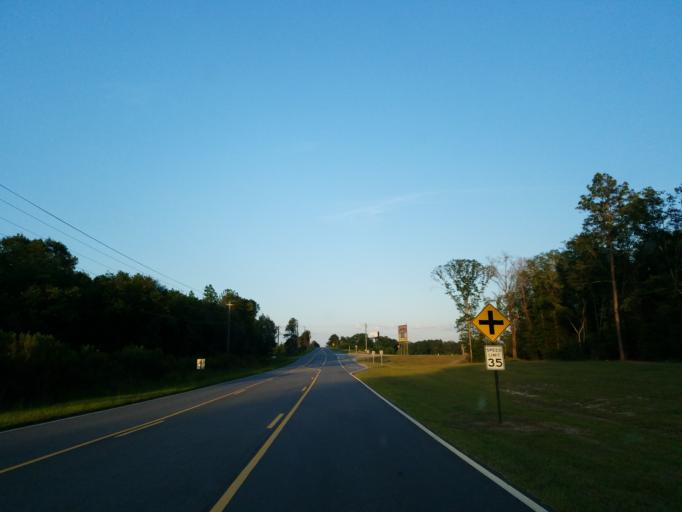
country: US
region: Georgia
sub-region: Crisp County
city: Cordele
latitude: 31.9257
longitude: -83.7490
